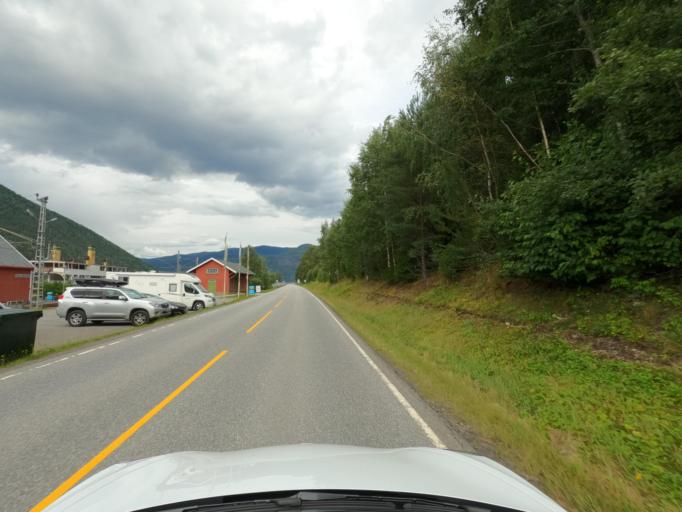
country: NO
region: Telemark
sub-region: Tinn
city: Rjukan
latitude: 59.9292
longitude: 8.8115
